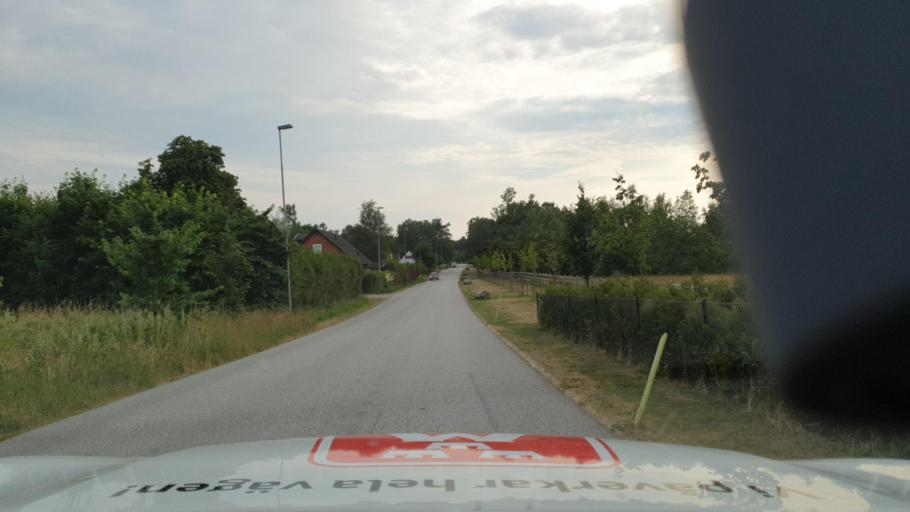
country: SE
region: Skane
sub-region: Sjobo Kommun
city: Sjoebo
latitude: 55.6314
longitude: 13.7294
